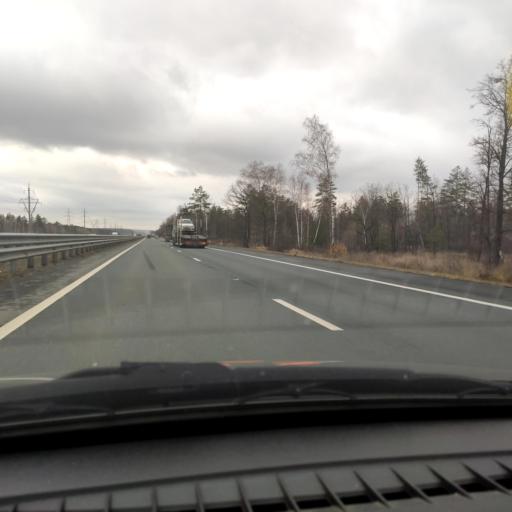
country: RU
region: Samara
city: Povolzhskiy
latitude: 53.5162
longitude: 49.7131
